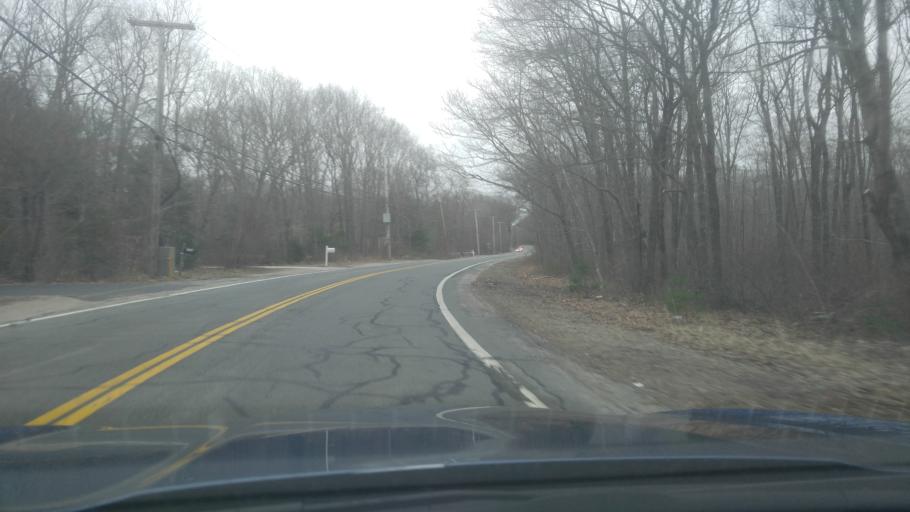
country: US
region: Rhode Island
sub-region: Kent County
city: Coventry
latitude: 41.6816
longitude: -71.6629
